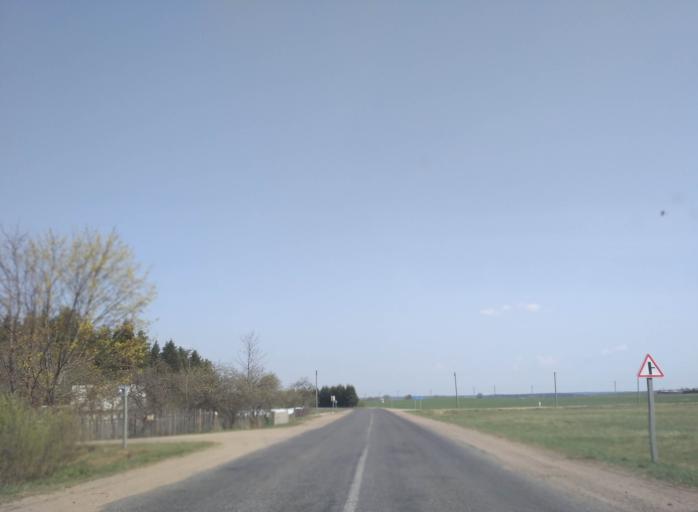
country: BY
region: Minsk
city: Horad Barysaw
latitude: 54.2913
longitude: 28.5281
